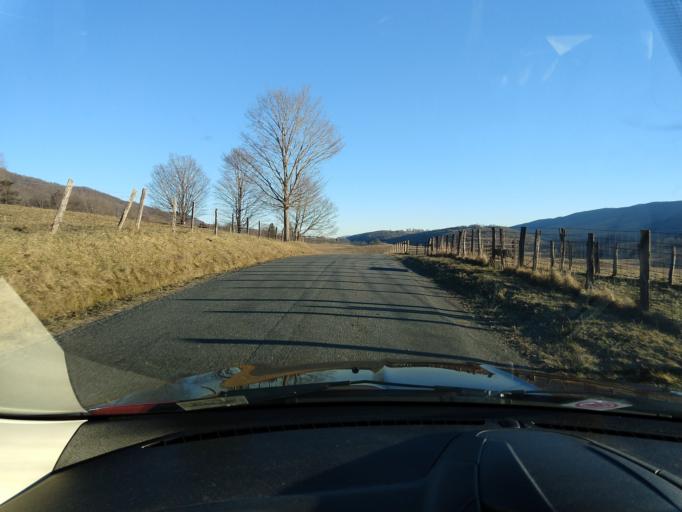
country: US
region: Virginia
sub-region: Highland County
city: Monterey
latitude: 38.4019
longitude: -79.6548
